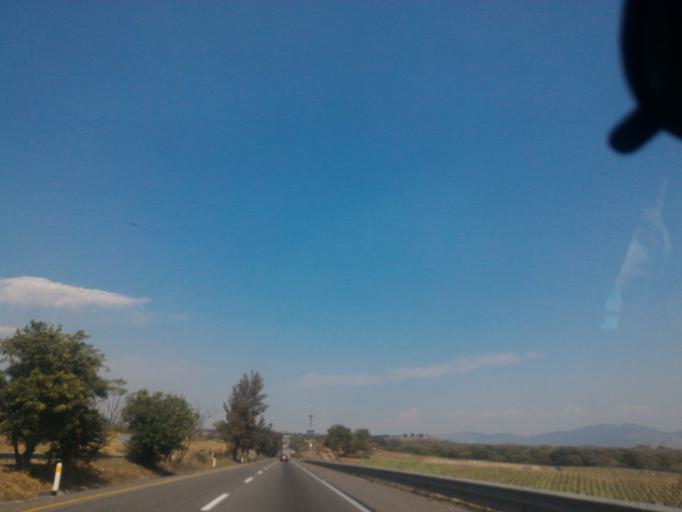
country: MX
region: Colima
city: Queseria
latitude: 19.3841
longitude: -103.5543
